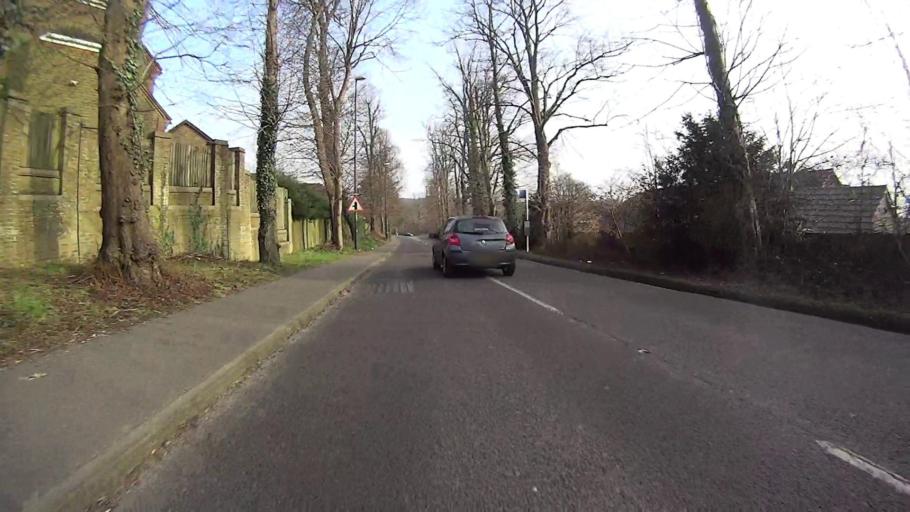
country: GB
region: England
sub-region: West Sussex
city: Maidenbower
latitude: 51.1102
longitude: -0.1459
